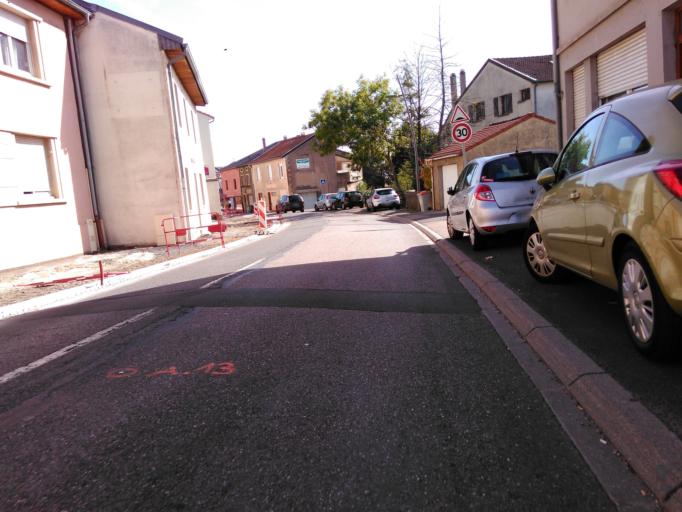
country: FR
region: Lorraine
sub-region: Departement de la Moselle
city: Hettange-Grande
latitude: 49.4064
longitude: 6.1502
